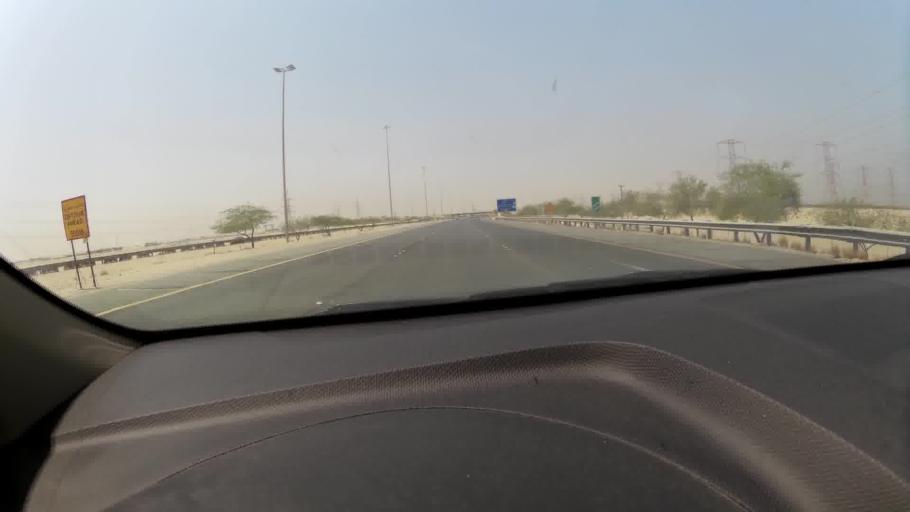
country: KW
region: Al Ahmadi
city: Al Fahahil
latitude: 28.9537
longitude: 48.1284
